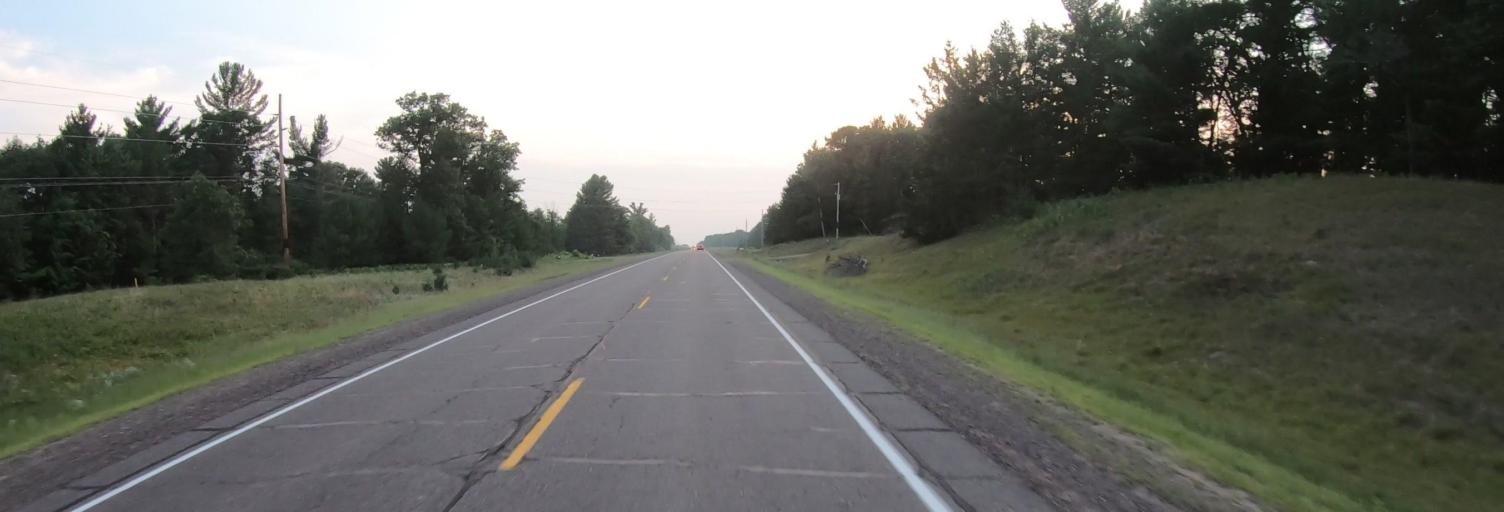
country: US
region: Wisconsin
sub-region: Burnett County
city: Grantsburg
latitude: 45.7732
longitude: -92.7263
